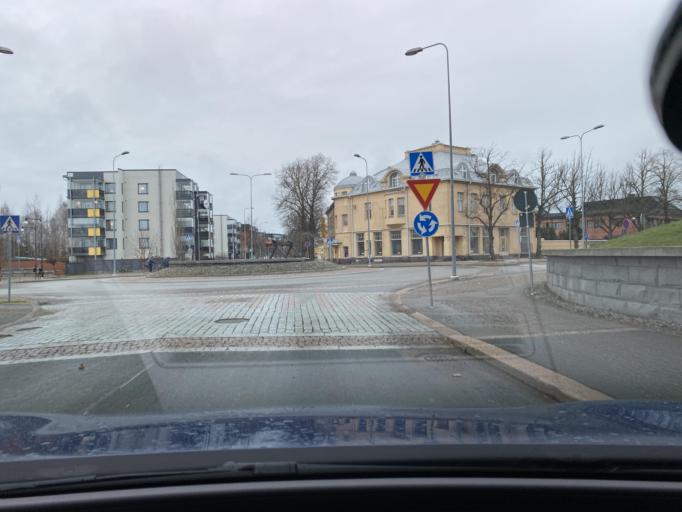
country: FI
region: Satakunta
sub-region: Rauma
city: Rauma
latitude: 61.1322
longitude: 21.4962
